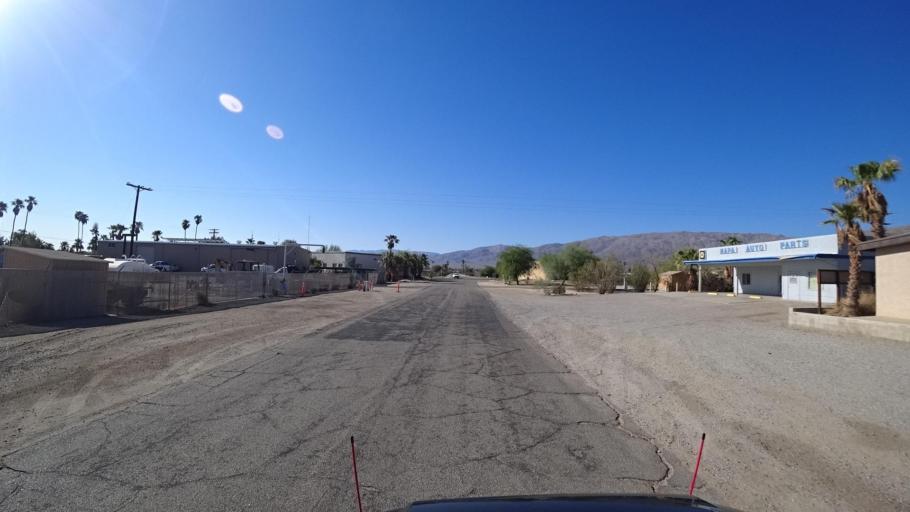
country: US
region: California
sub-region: San Diego County
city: Borrego Springs
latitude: 33.2578
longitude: -116.3712
